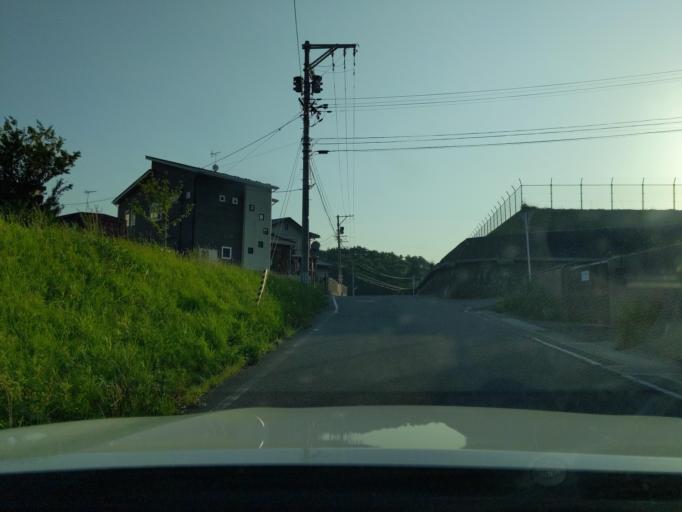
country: JP
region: Fukushima
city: Motomiya
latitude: 37.4845
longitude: 140.3630
